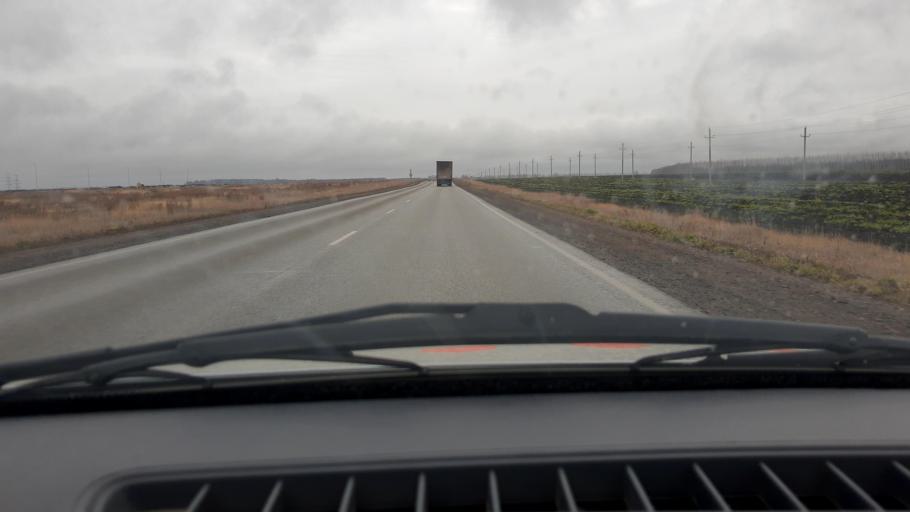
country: RU
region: Bashkortostan
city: Iglino
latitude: 54.7588
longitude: 56.2758
